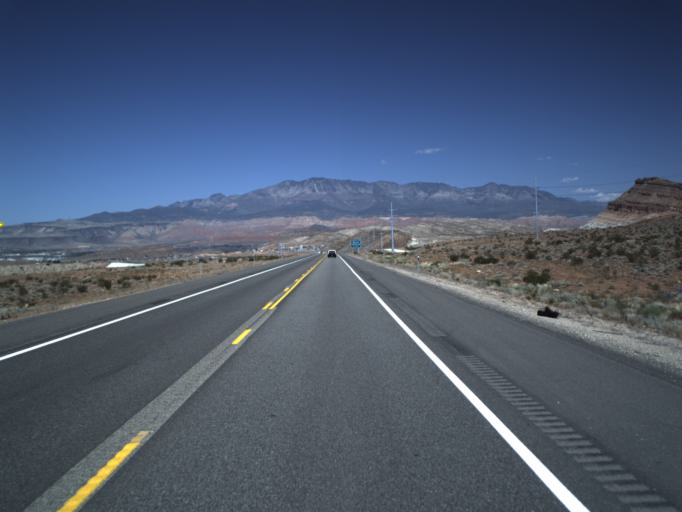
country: US
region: Utah
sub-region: Washington County
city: Washington
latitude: 37.0475
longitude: -113.4857
